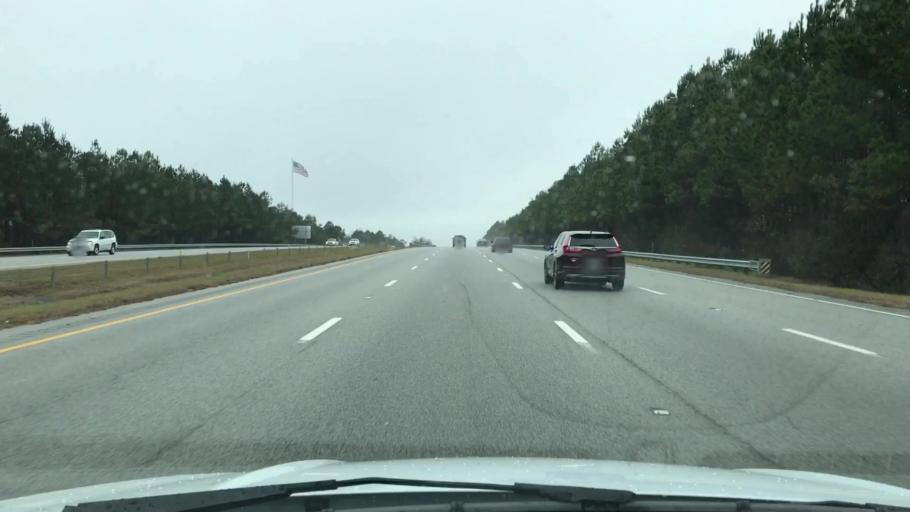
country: US
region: South Carolina
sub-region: Horry County
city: Myrtle Beach
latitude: 33.7515
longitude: -78.8654
